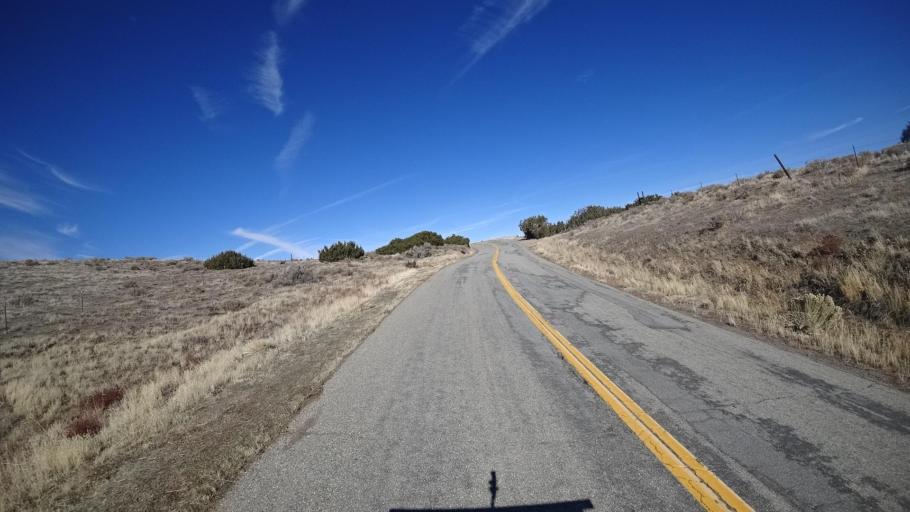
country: US
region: California
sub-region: Kern County
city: Pine Mountain Club
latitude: 34.8729
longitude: -119.2849
